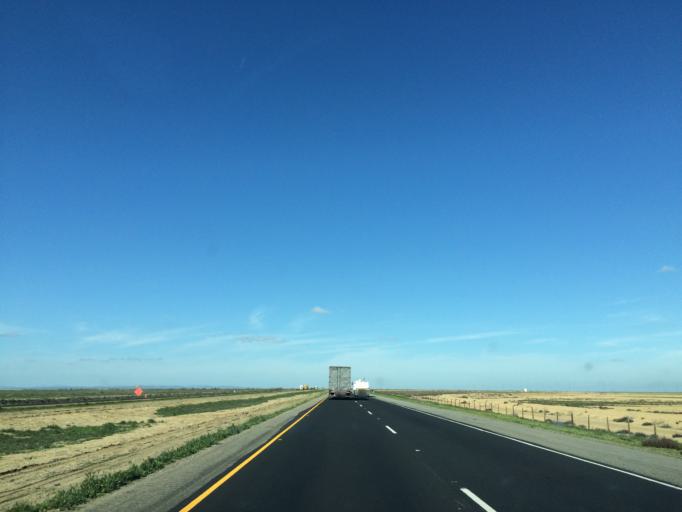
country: US
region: California
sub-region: Kern County
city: Lost Hills
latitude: 35.7537
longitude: -119.7554
